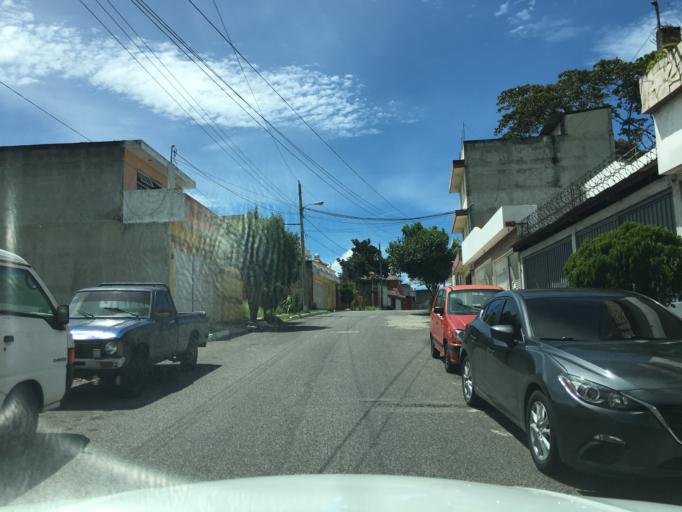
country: GT
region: Guatemala
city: Mixco
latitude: 14.6564
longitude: -90.5649
